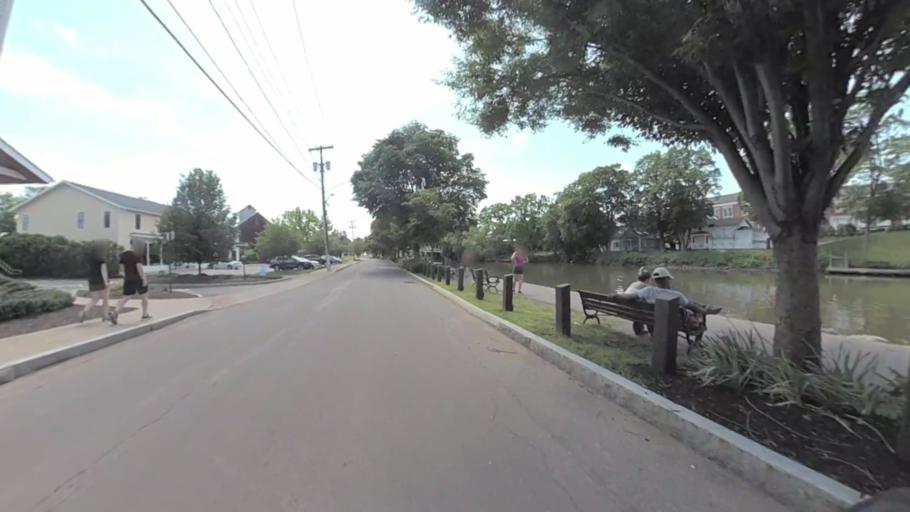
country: US
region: New York
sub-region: Monroe County
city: Pittsford
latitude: 43.0913
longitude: -77.5123
